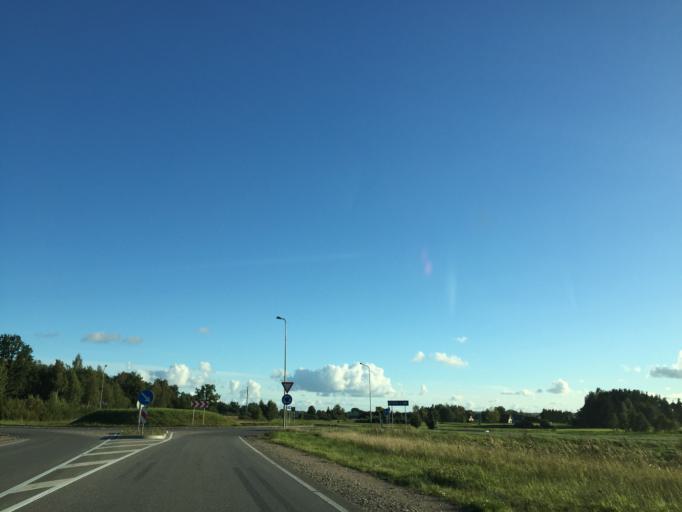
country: LV
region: Kuldigas Rajons
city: Kuldiga
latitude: 56.9727
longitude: 22.0154
